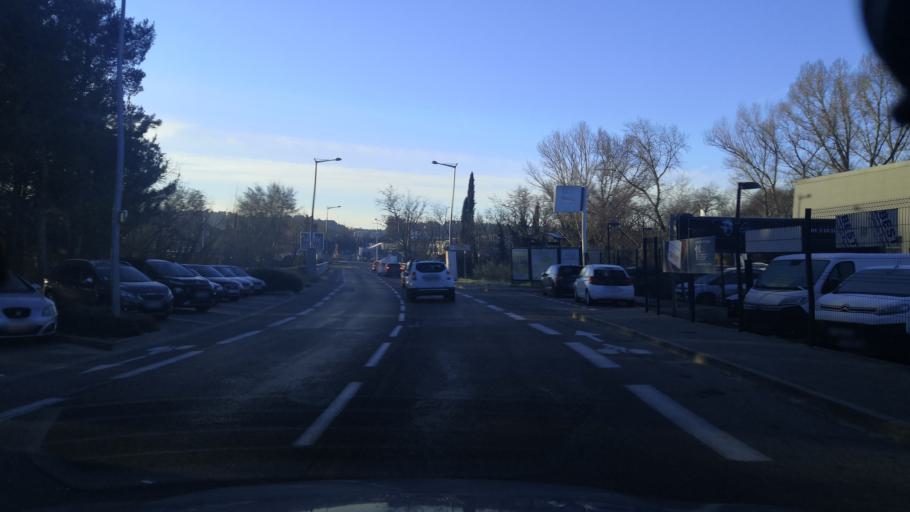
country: FR
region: Provence-Alpes-Cote d'Azur
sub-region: Departement des Bouches-du-Rhone
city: Aix-en-Provence
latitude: 43.5096
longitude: 5.4090
